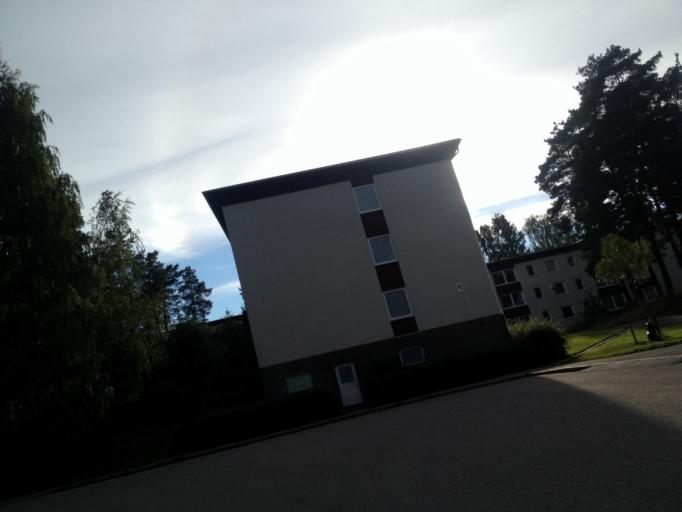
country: SE
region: Stockholm
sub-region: Sigtuna Kommun
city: Marsta
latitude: 59.6152
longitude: 17.8385
